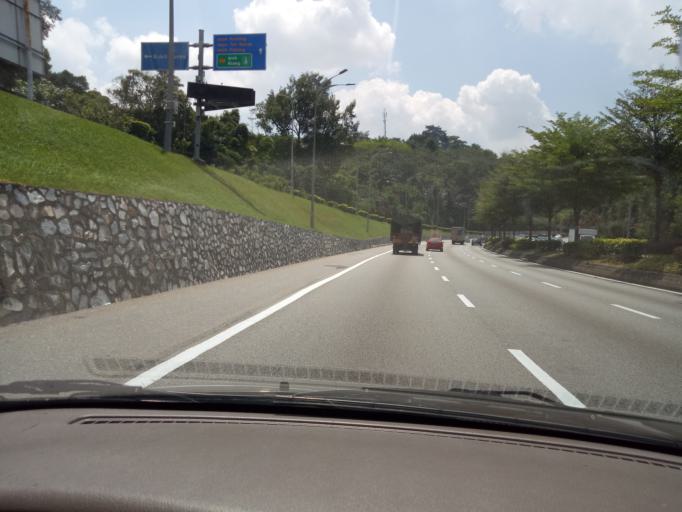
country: MY
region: Kuala Lumpur
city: Kuala Lumpur
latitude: 3.1578
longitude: 101.6812
